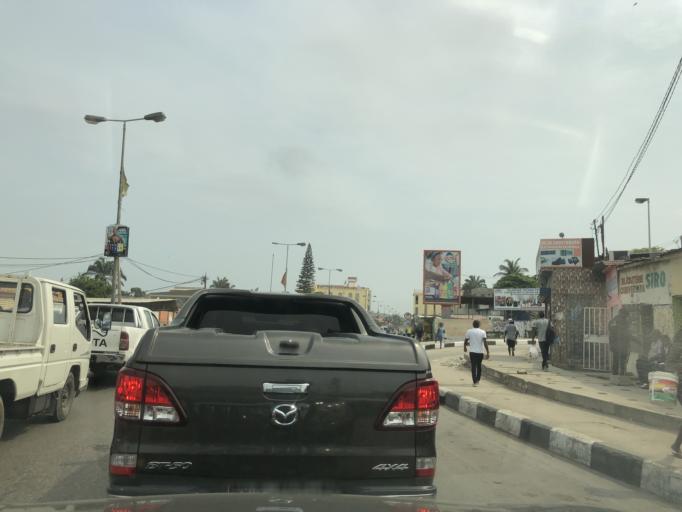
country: AO
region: Luanda
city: Luanda
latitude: -8.8452
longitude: 13.2124
